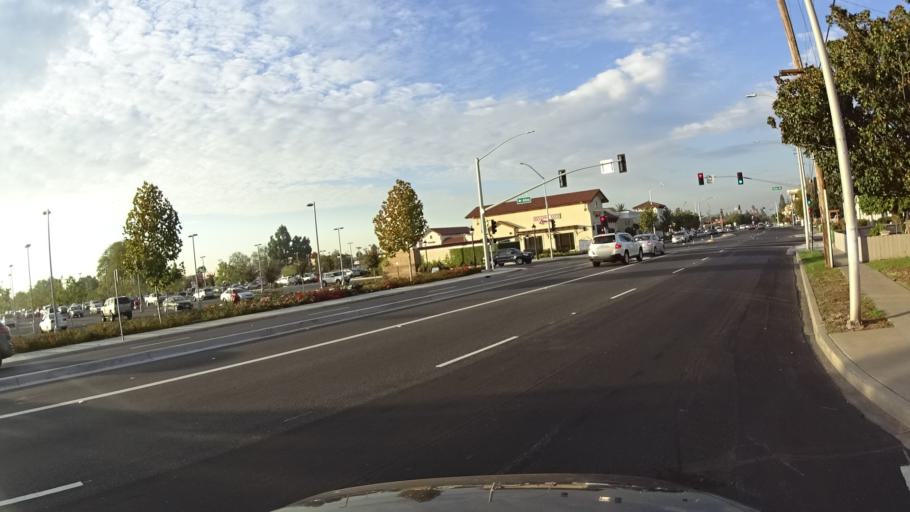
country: US
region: California
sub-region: Santa Clara County
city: Santa Clara
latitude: 37.3507
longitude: -121.9593
